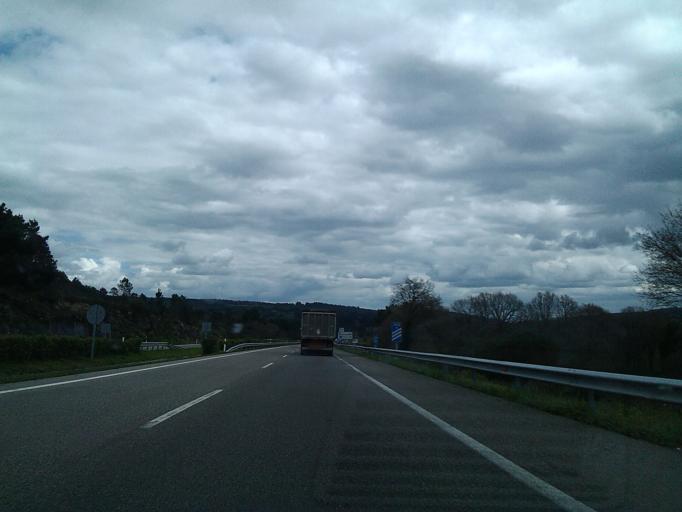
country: ES
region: Galicia
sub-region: Provincia de Lugo
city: Guitiriz
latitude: 43.1857
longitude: -7.8340
